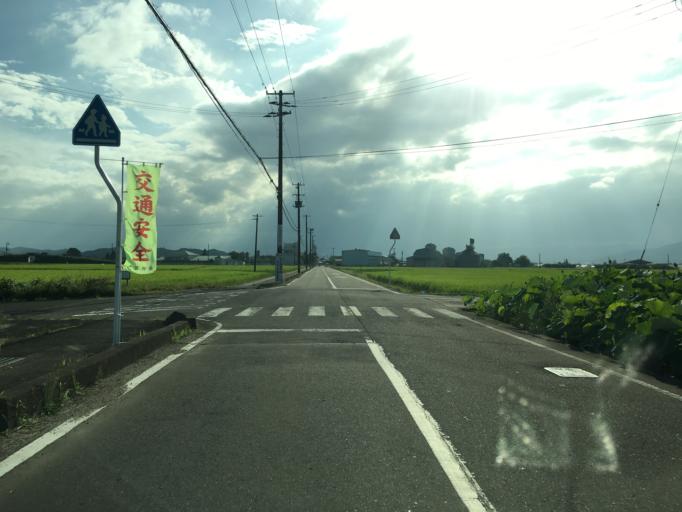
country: JP
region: Fukushima
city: Hobaramachi
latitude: 37.8275
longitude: 140.5787
